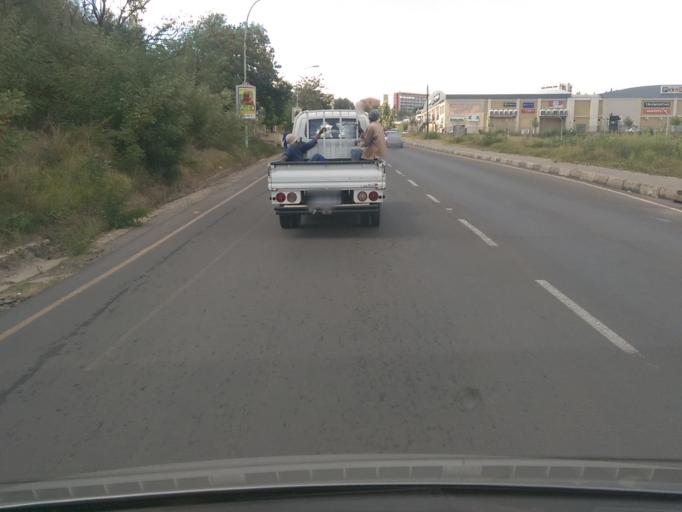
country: LS
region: Maseru
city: Maseru
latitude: -29.3176
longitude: 27.4753
